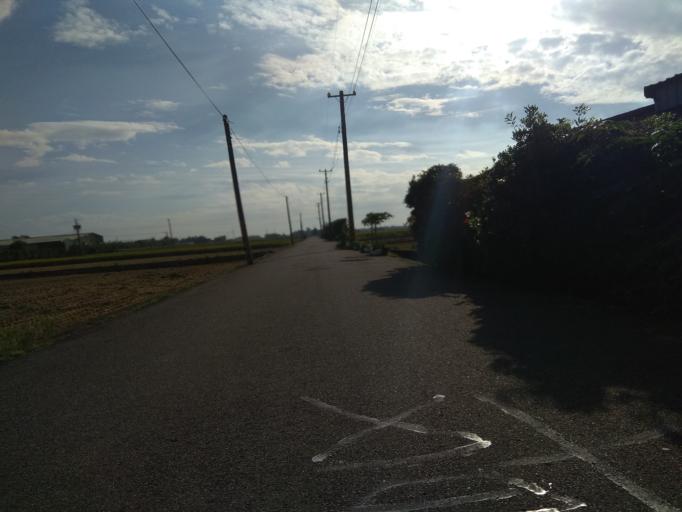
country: TW
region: Taiwan
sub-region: Hsinchu
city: Zhubei
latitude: 24.9814
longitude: 121.0475
